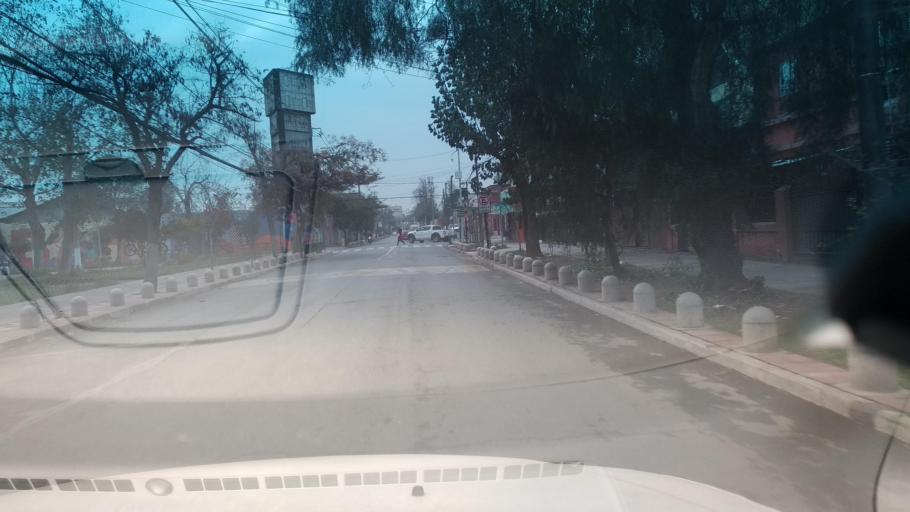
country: CL
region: Santiago Metropolitan
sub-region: Provincia de Santiago
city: Santiago
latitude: -33.4577
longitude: -70.6840
